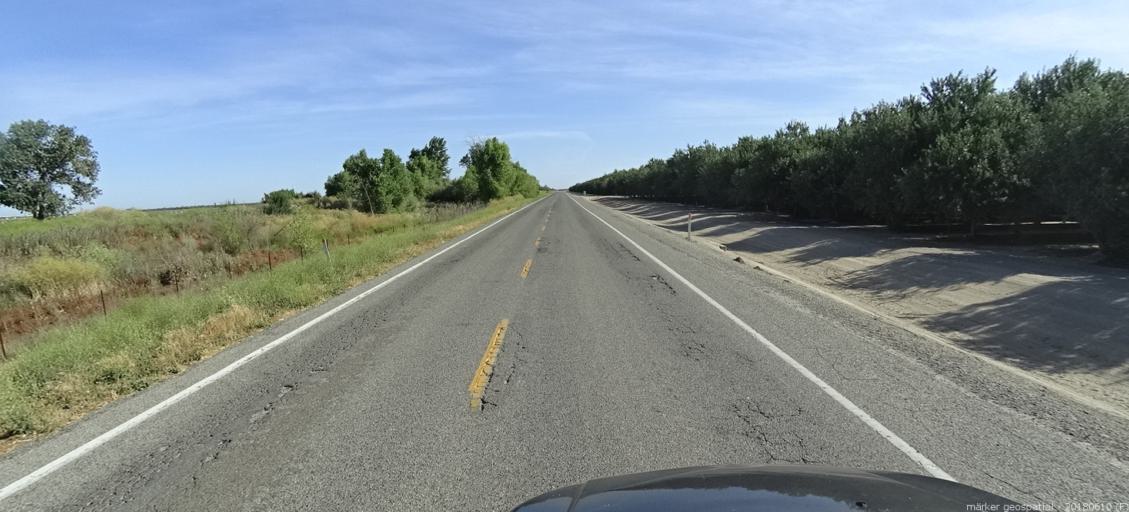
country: US
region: California
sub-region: Madera County
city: Fairmead
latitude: 36.9731
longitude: -120.2559
